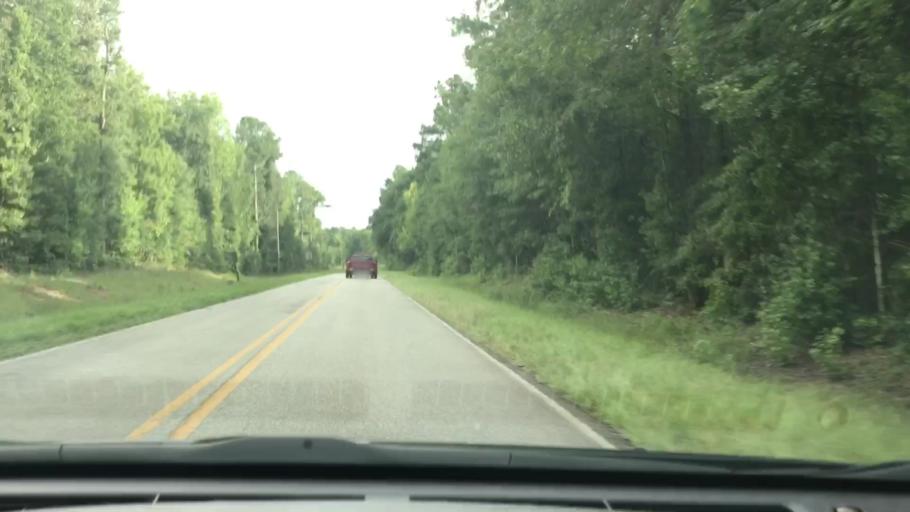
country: US
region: Georgia
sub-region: Jefferson County
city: Wadley
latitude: 32.8172
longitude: -82.3764
